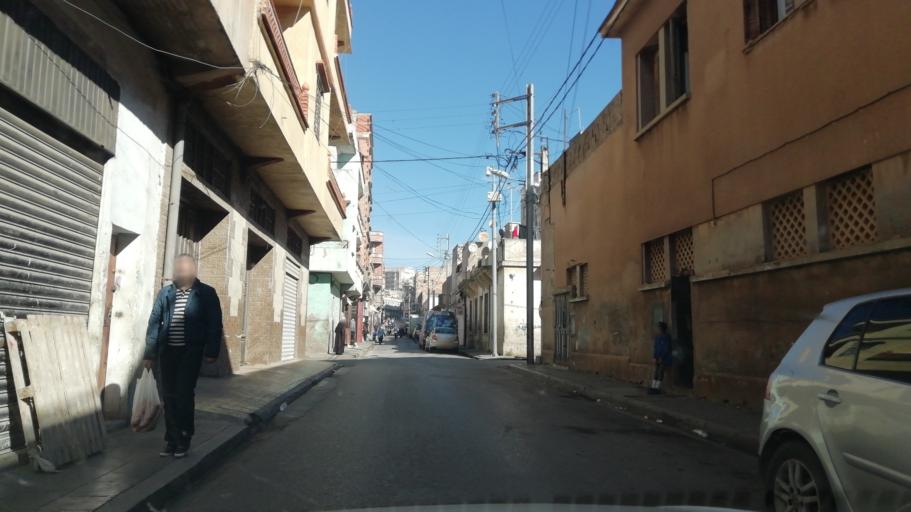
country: DZ
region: Oran
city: Oran
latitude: 35.6970
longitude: -0.6237
